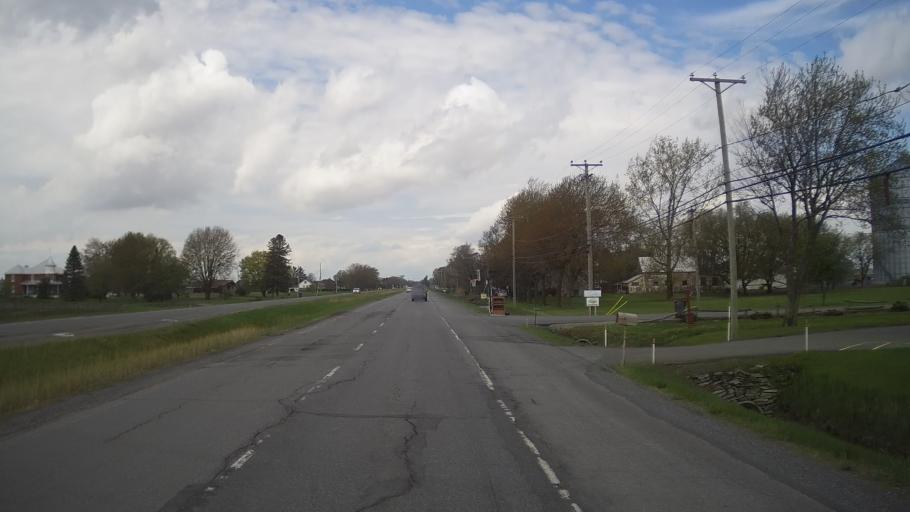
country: CA
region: Quebec
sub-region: Monteregie
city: Saint-Jean-sur-Richelieu
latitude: 45.3652
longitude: -73.3213
